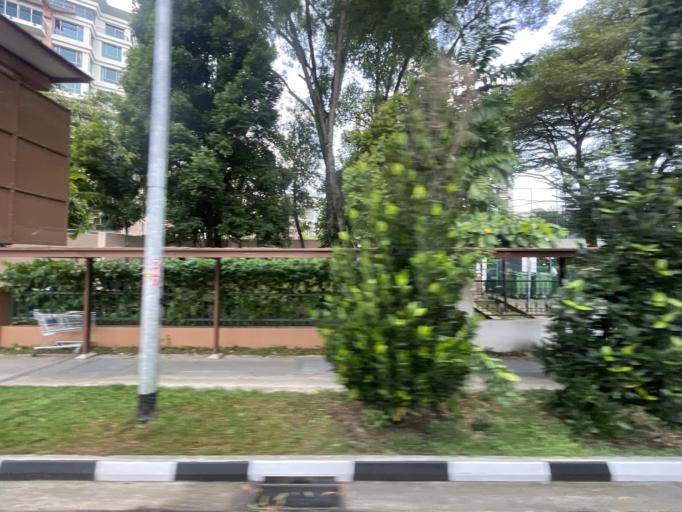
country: SG
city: Singapore
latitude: 1.3355
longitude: 103.7840
